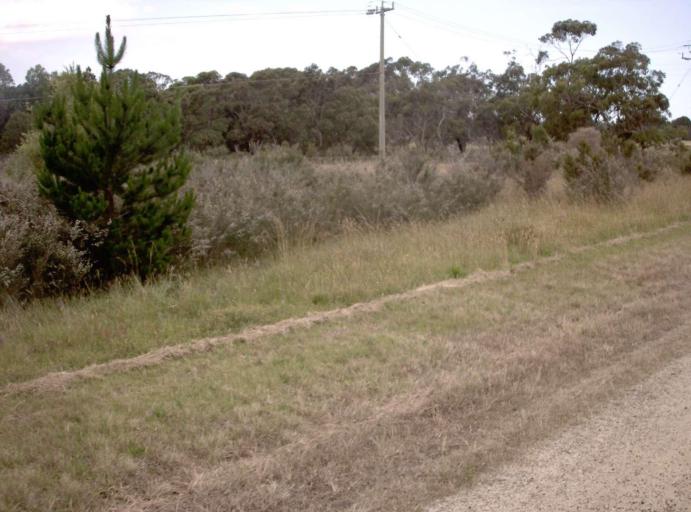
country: AU
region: Victoria
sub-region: Wellington
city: Sale
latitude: -38.1996
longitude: 147.0963
